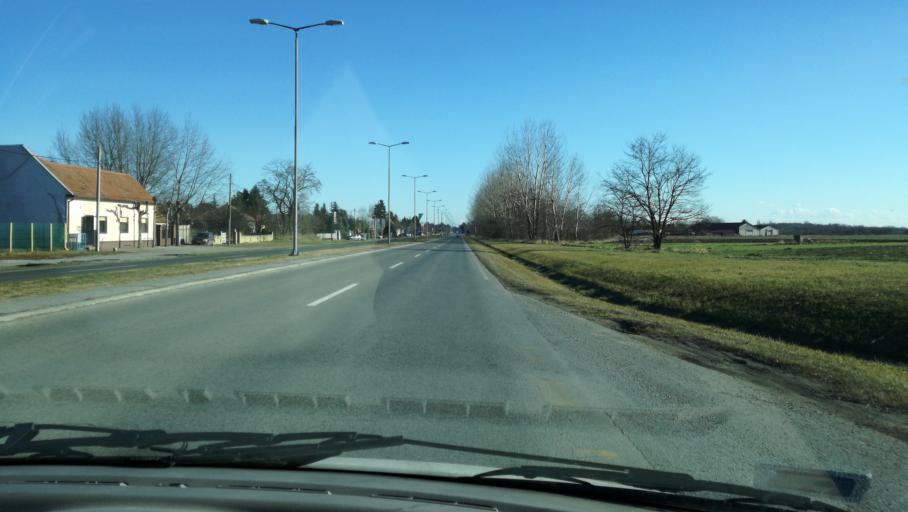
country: RS
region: Autonomna Pokrajina Vojvodina
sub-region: Severnobacki Okrug
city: Subotica
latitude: 46.1048
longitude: 19.7303
